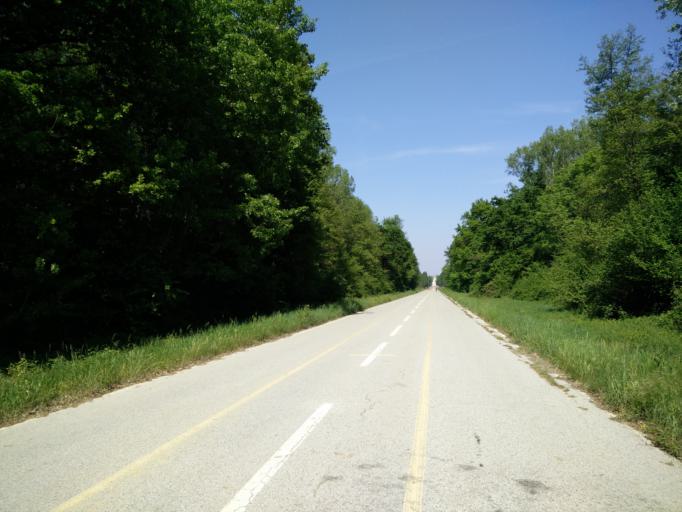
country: IT
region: Piedmont
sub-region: Provincia di Torino
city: Candiolo
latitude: 44.9850
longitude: 7.5929
